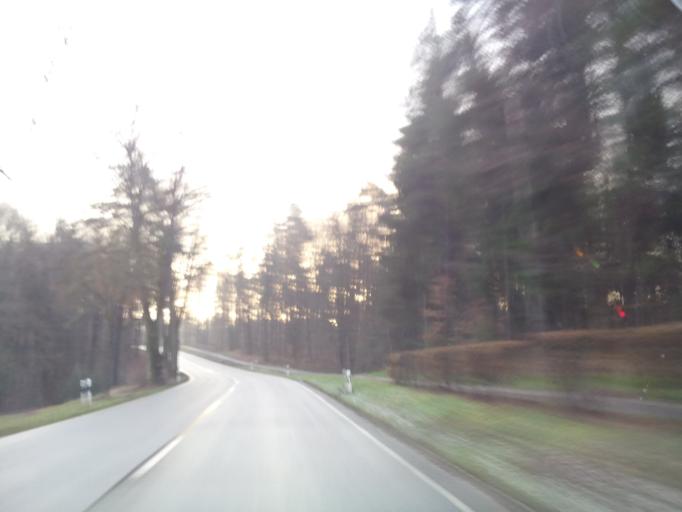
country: DE
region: Bavaria
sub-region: Upper Franconia
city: Lichtenfels
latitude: 50.1723
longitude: 11.0289
